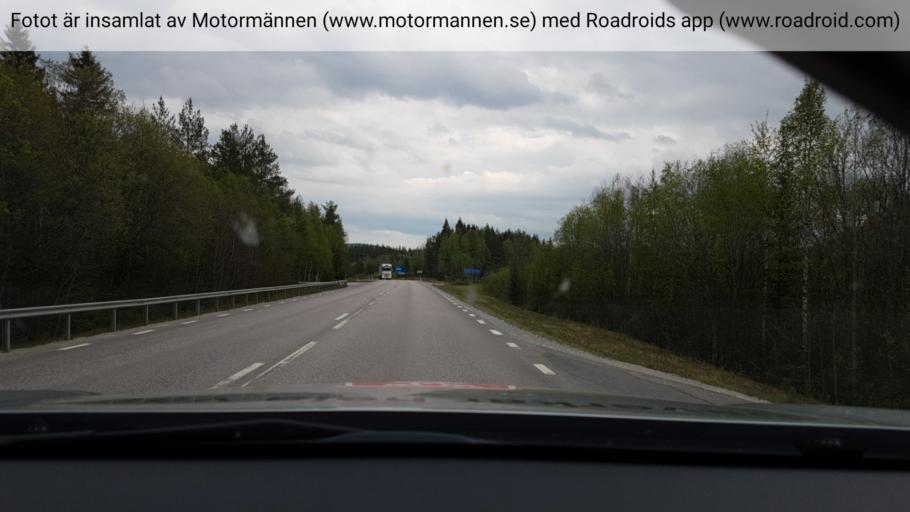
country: SE
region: Vaesterbotten
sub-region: Vannas Kommun
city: Vaennaes
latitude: 63.9052
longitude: 19.6763
